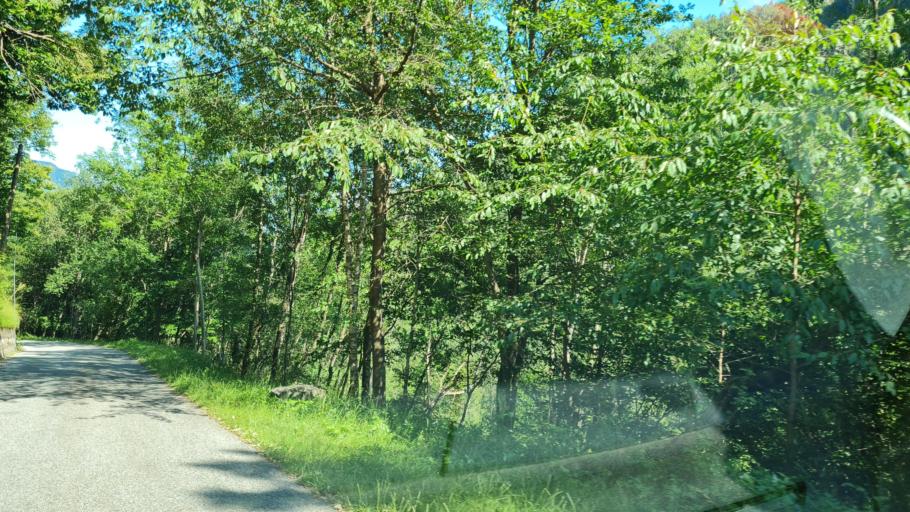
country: IT
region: Piedmont
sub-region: Provincia di Torino
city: Quincinetto
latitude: 45.5548
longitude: 7.7866
